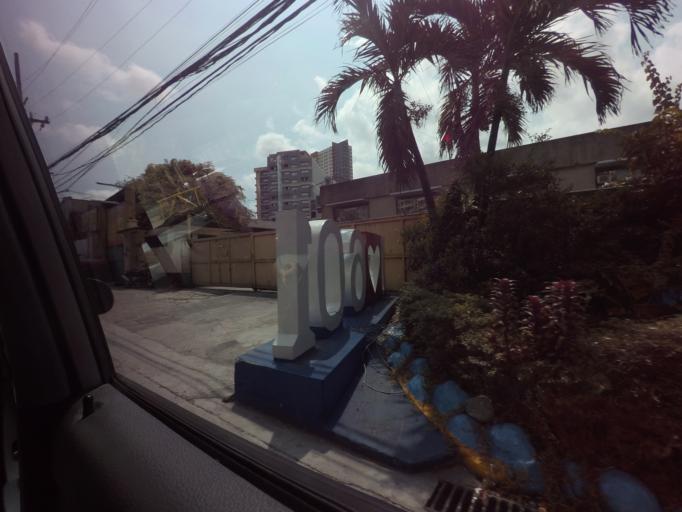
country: PH
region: Metro Manila
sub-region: San Juan
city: San Juan
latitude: 14.5963
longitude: 121.0207
